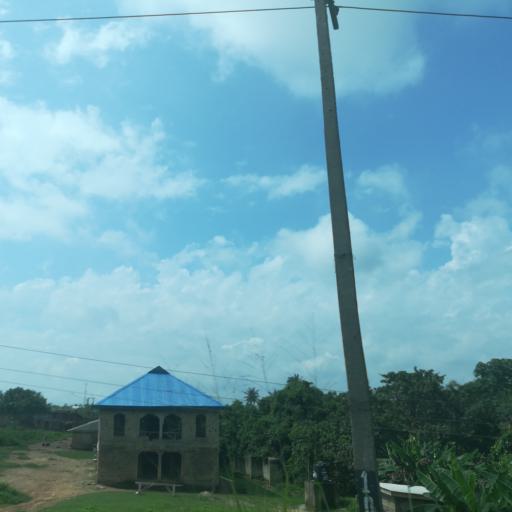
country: NG
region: Lagos
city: Ikorodu
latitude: 6.6715
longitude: 3.6660
